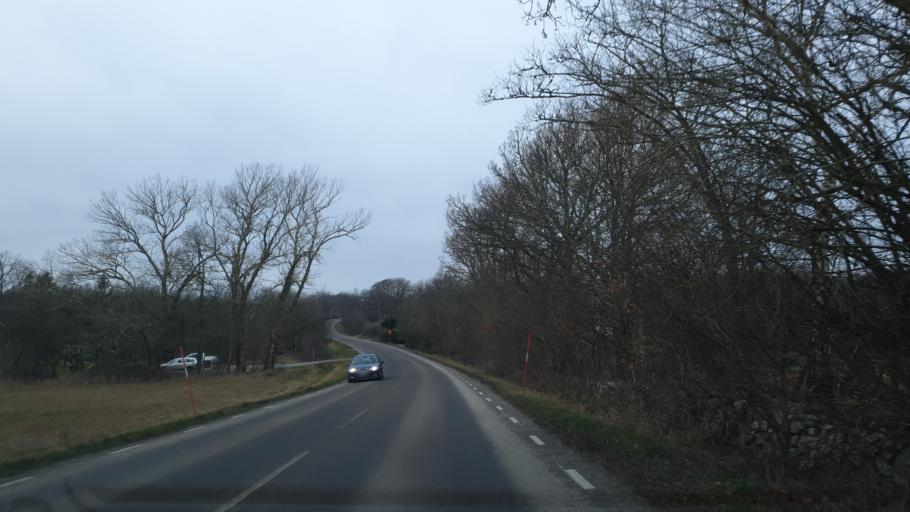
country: SE
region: Blekinge
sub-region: Karlskrona Kommun
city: Sturko
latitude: 56.1127
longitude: 15.7004
